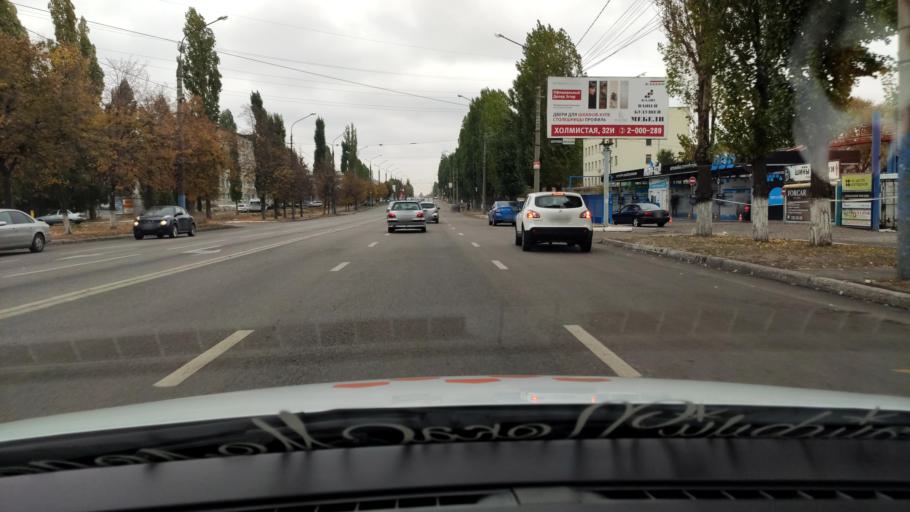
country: RU
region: Voronezj
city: Voronezh
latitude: 51.6820
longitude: 39.1661
